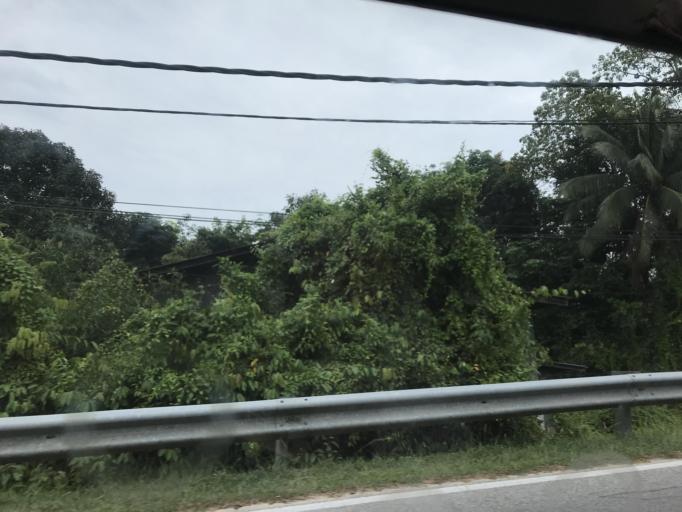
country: MY
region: Kelantan
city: Kota Bharu
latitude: 6.1636
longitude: 102.2264
